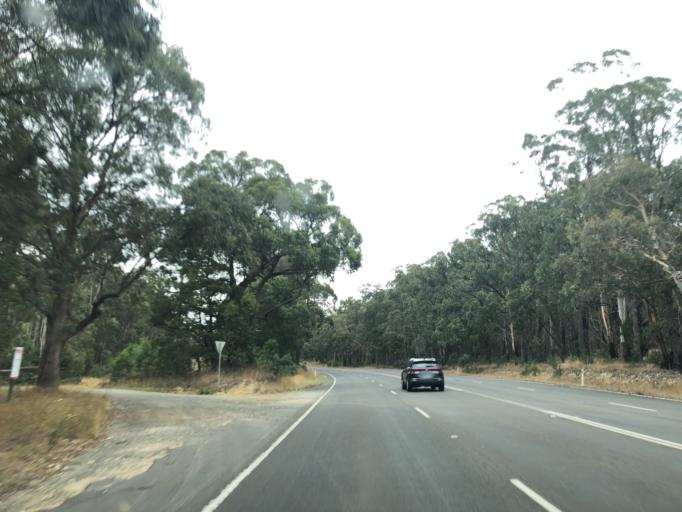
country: AU
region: Victoria
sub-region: Hume
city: Sunbury
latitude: -37.3913
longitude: 144.5269
